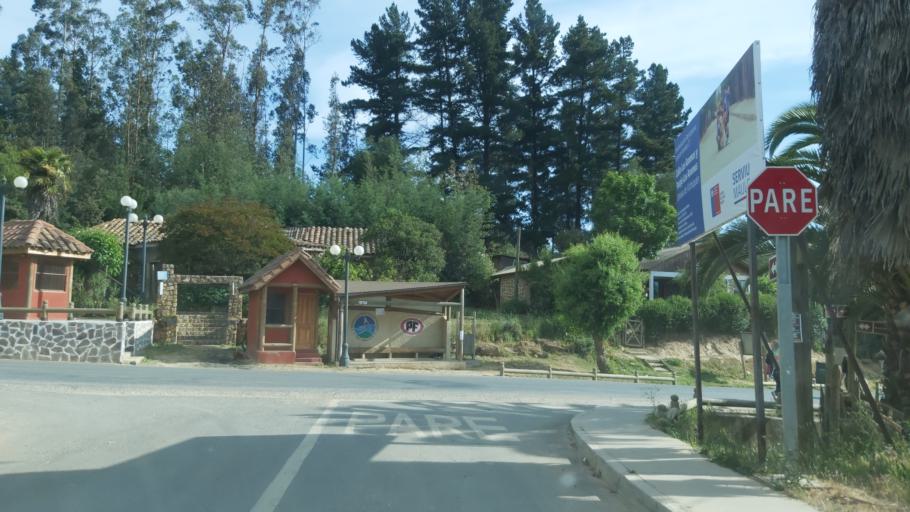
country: CL
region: Maule
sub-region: Provincia de Talca
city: Constitucion
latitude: -34.8508
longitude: -72.0381
